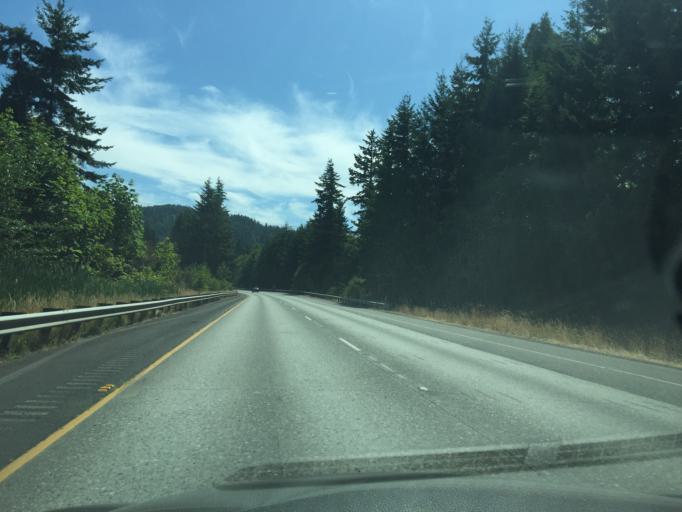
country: US
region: Washington
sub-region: Whatcom County
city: Bellingham
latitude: 48.7094
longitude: -122.4767
